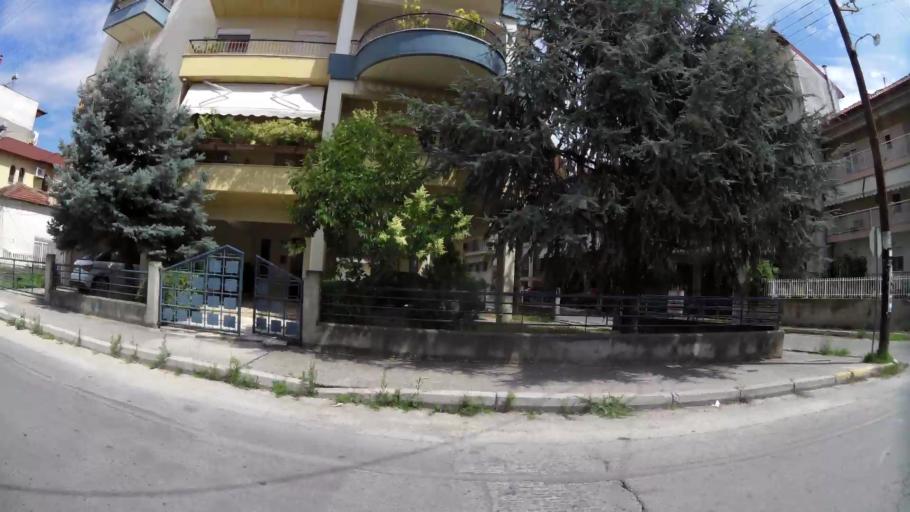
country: GR
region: Central Macedonia
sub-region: Nomos Pierias
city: Katerini
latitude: 40.2698
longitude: 22.4956
